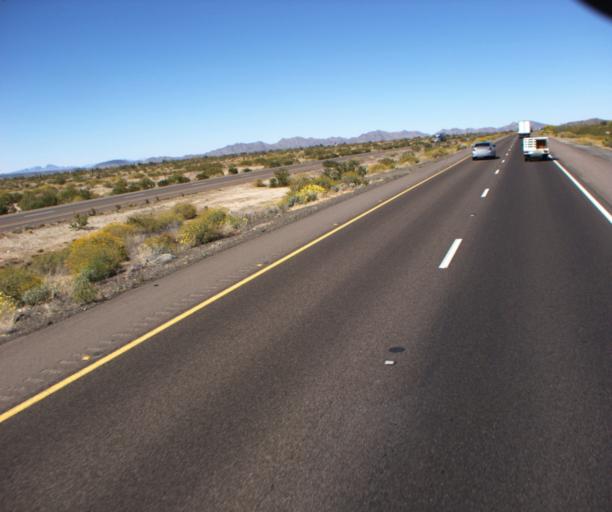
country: US
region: Arizona
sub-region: Maricopa County
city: Gila Bend
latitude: 33.1200
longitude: -112.6498
